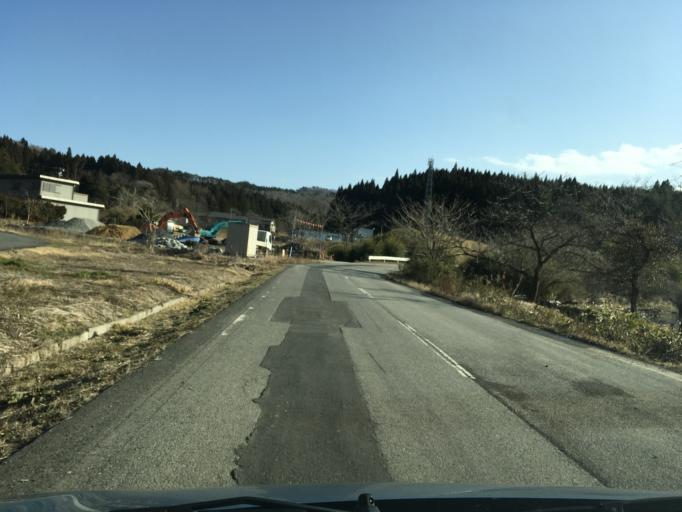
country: JP
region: Miyagi
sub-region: Oshika Gun
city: Onagawa Cho
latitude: 38.7831
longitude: 141.4587
